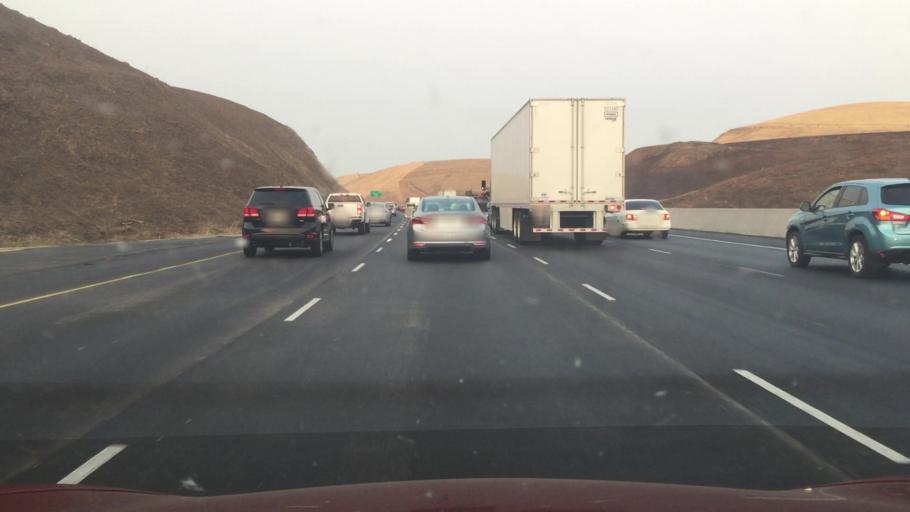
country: US
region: California
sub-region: San Joaquin County
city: Mountain House
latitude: 37.7352
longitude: -121.6120
